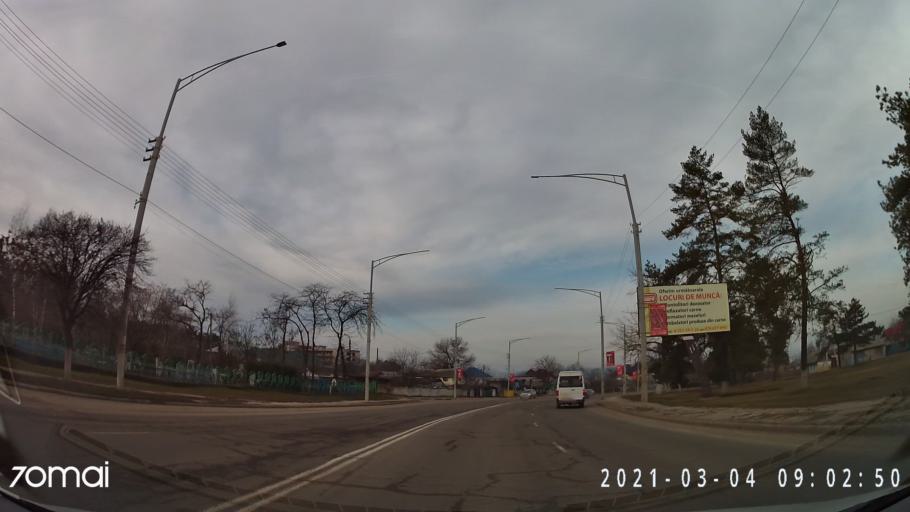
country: MD
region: Balti
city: Balti
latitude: 47.7453
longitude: 27.9507
